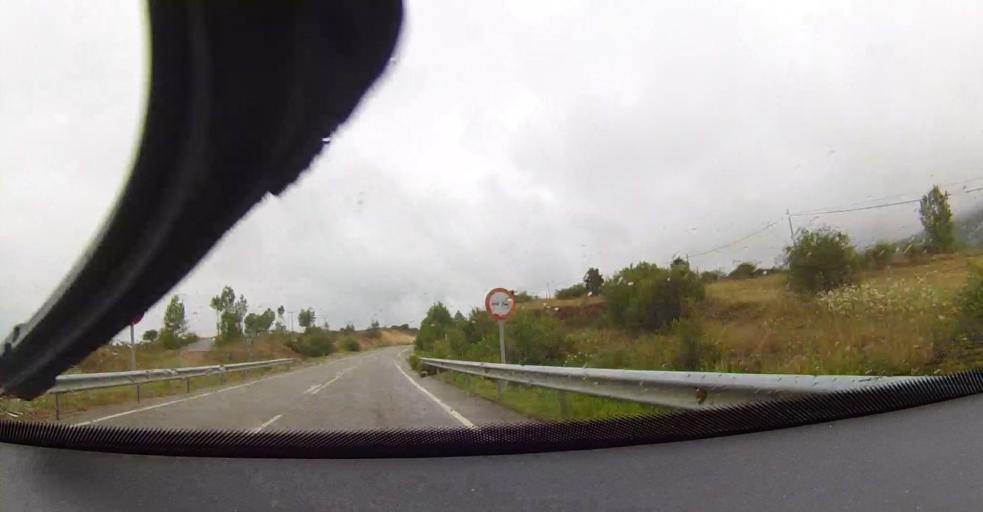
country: ES
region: Castille and Leon
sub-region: Provincia de Leon
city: Bonar
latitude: 42.8461
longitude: -5.2677
